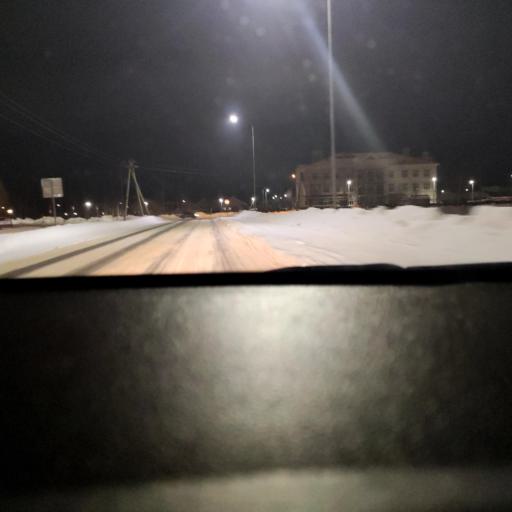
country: RU
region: Tatarstan
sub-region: Chistopol'skiy Rayon
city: Chistopol'
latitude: 55.3611
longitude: 50.5825
